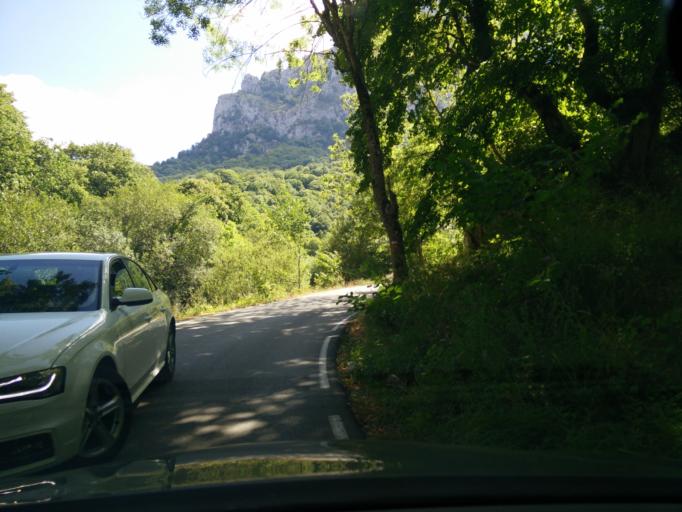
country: ES
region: Castille and Leon
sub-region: Provincia de Leon
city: Posada de Valdeon
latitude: 43.1941
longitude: -4.9074
